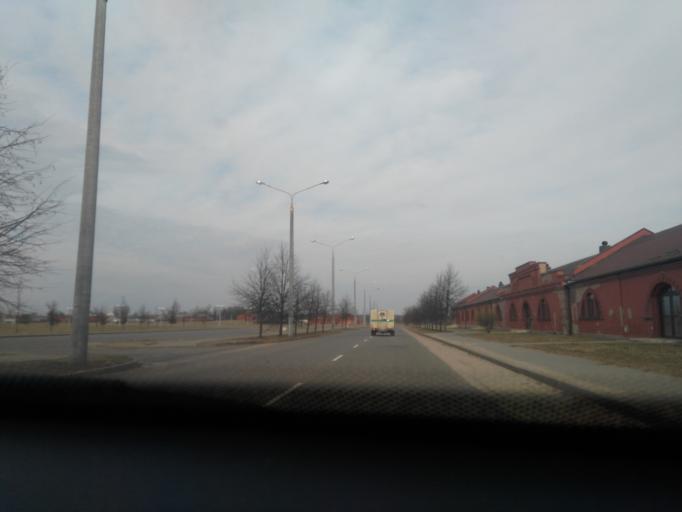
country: BY
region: Mogilev
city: Babruysk
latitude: 53.1402
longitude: 29.2481
